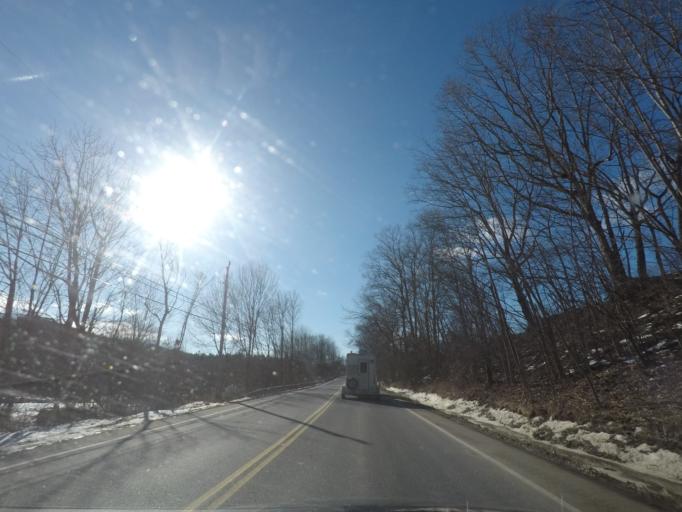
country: US
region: New York
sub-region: Columbia County
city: Chatham
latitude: 42.4207
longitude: -73.4990
